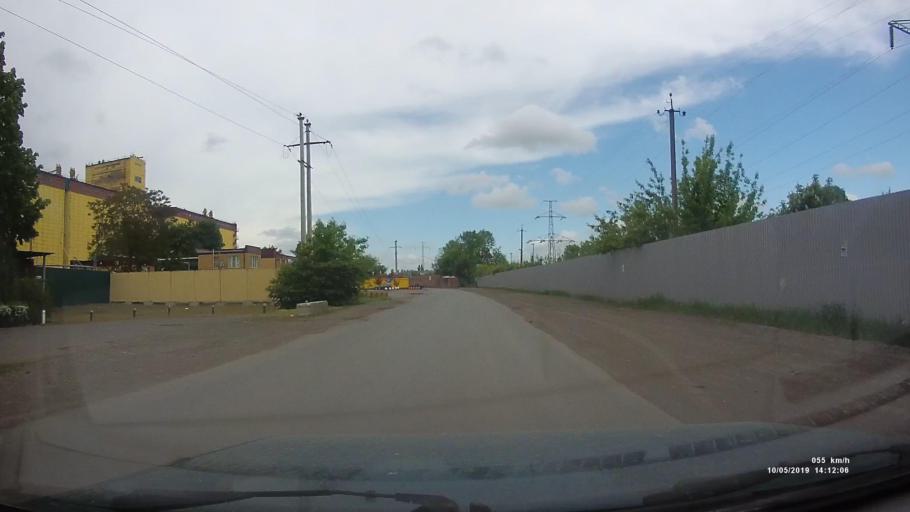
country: RU
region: Rostov
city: Azov
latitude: 47.0935
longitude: 39.4223
